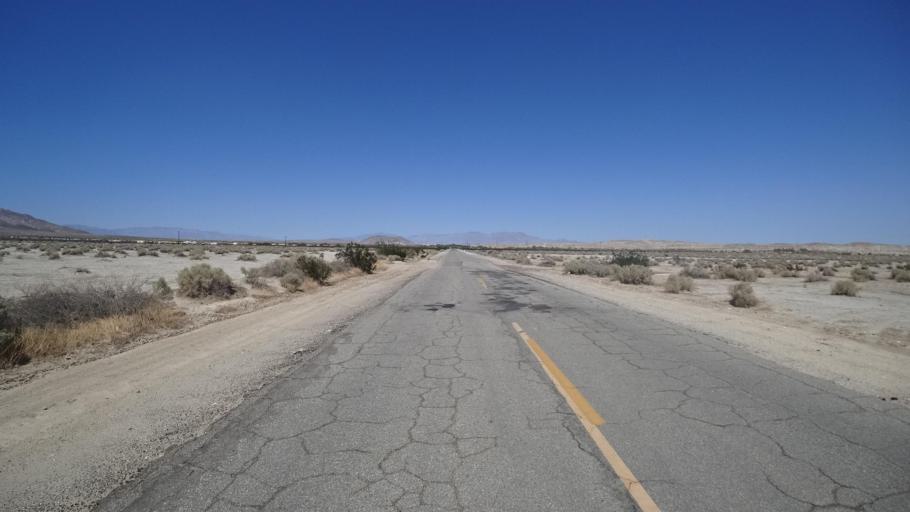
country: US
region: California
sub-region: Imperial County
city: Salton City
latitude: 33.0943
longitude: -116.1130
